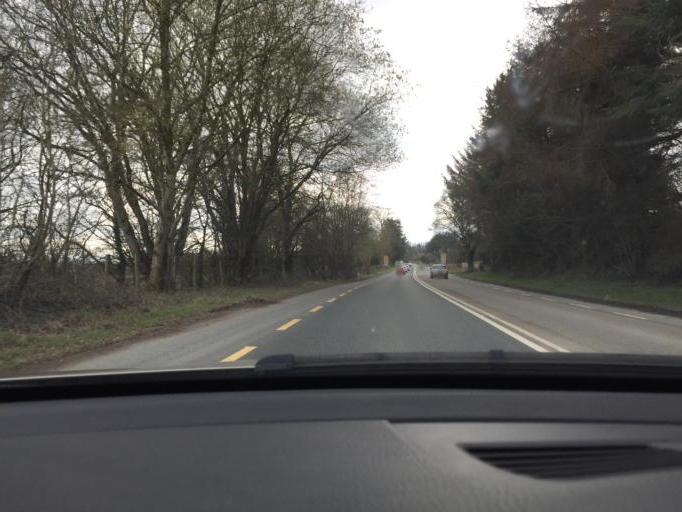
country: IE
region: Leinster
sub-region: Wicklow
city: Blessington
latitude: 53.2085
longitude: -6.4896
